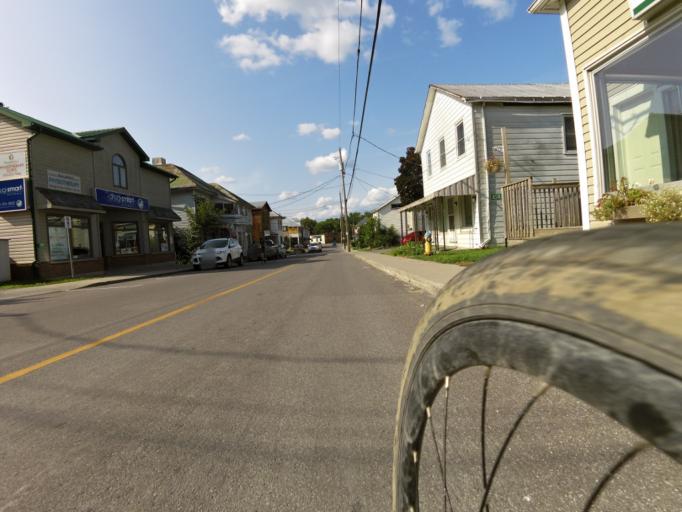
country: CA
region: Ontario
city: Kingston
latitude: 44.4097
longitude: -76.5965
